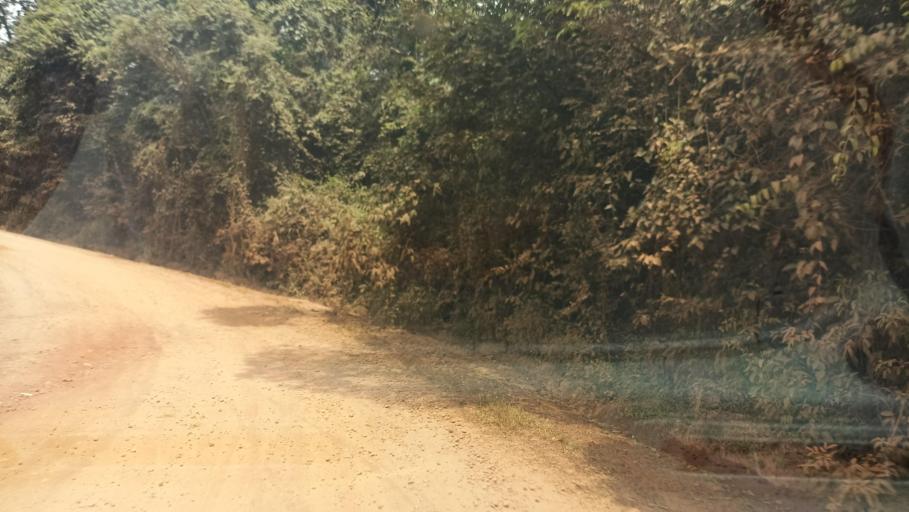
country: BR
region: Minas Gerais
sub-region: Itabirito
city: Itabirito
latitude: -20.3392
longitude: -43.7711
